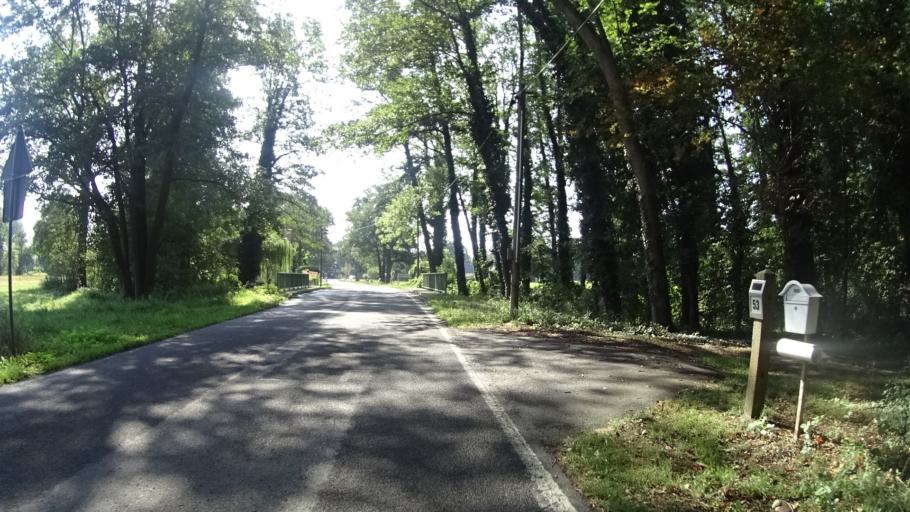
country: DE
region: Brandenburg
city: Burg
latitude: 51.8667
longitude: 14.1241
